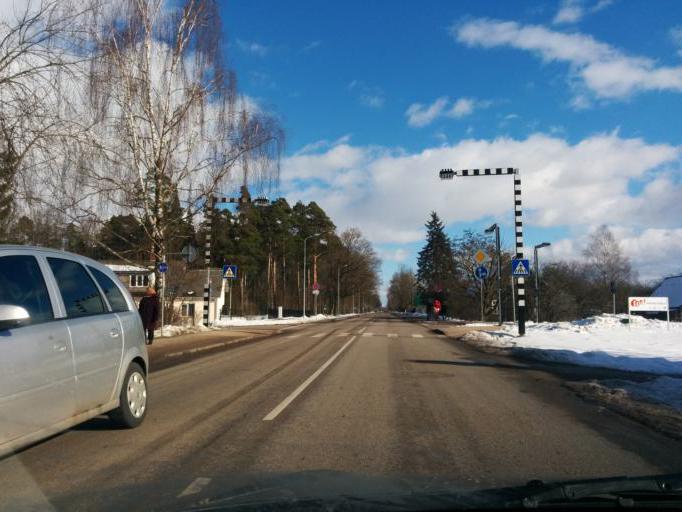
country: LV
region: Gulbenes Rajons
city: Gulbene
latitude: 57.1686
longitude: 26.7692
